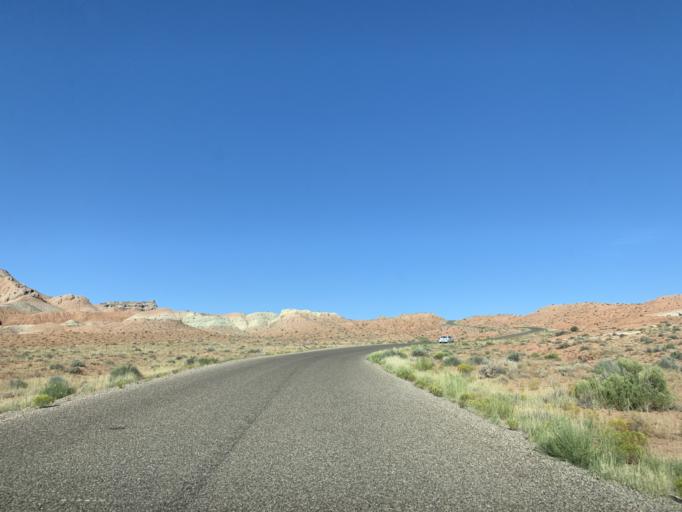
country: US
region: Utah
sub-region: Emery County
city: Ferron
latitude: 38.5808
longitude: -110.7777
